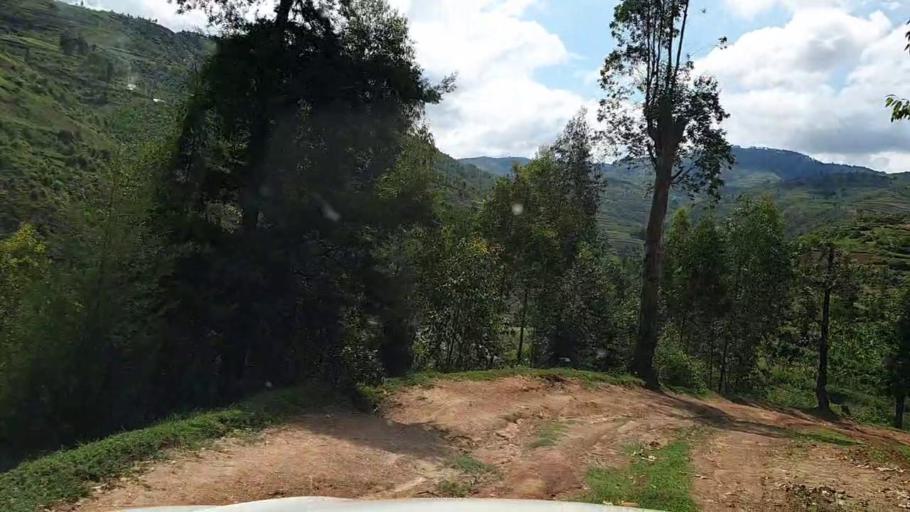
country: RW
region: Southern Province
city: Gikongoro
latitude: -2.3617
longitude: 29.5410
